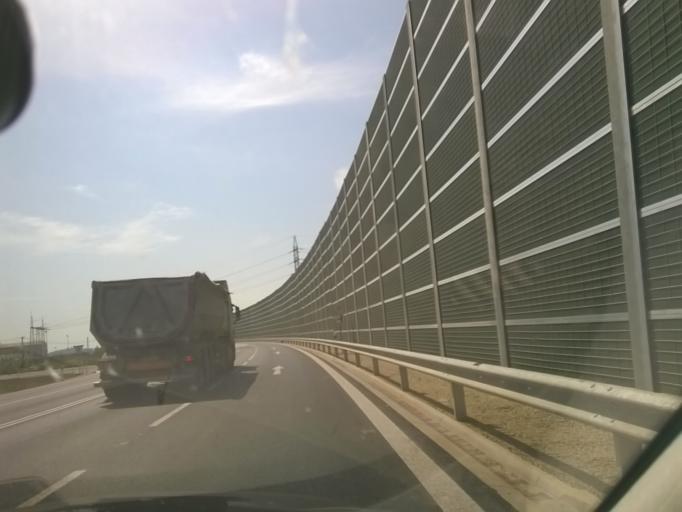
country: SK
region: Nitriansky
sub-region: Okres Nitra
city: Nitra
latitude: 48.3283
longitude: 18.0427
